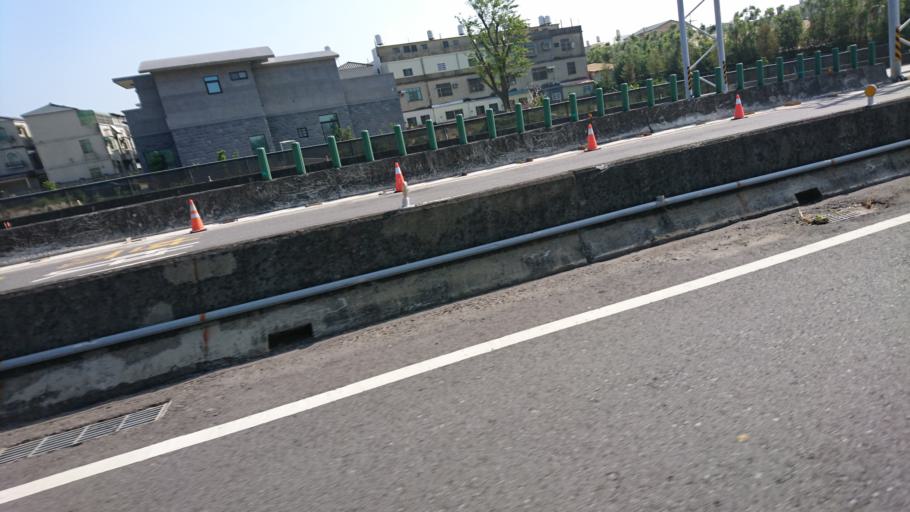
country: TW
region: Taiwan
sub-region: Miaoli
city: Miaoli
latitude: 24.6911
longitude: 120.8563
